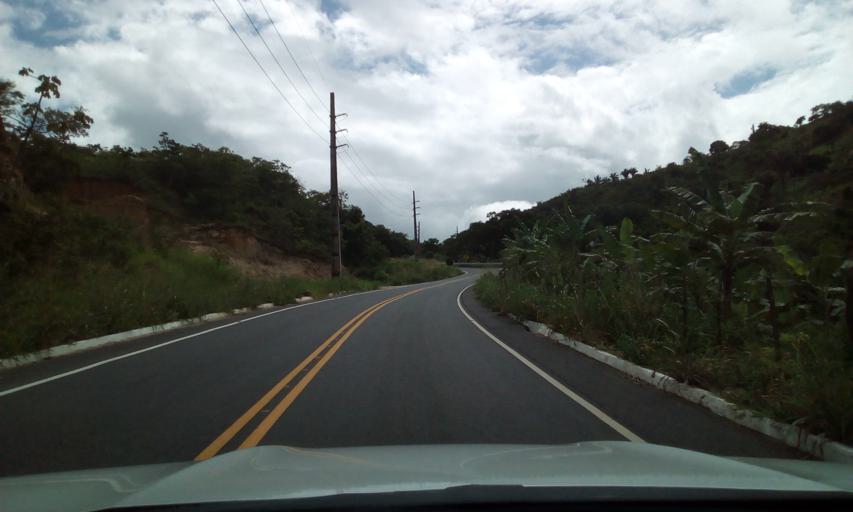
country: BR
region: Paraiba
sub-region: Alagoinha
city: Alagoinha
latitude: -6.8856
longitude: -35.5864
